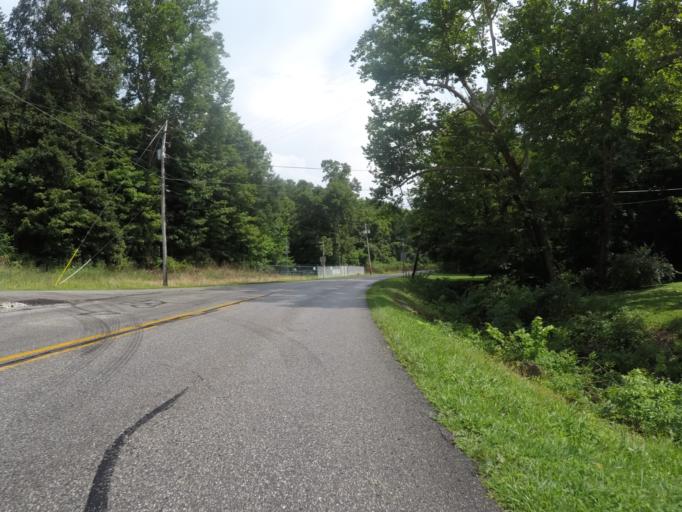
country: US
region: Kentucky
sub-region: Boyd County
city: Ironville
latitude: 38.4517
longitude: -82.6866
